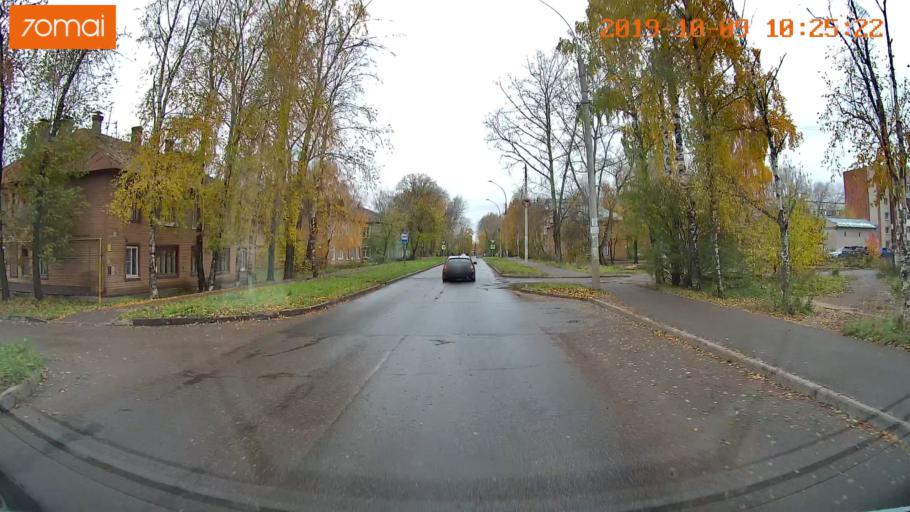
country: RU
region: Vologda
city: Vologda
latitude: 59.2131
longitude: 39.9296
